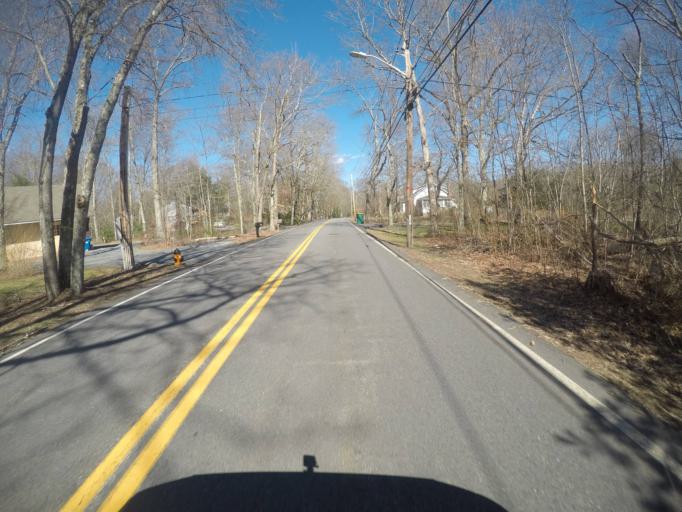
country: US
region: Massachusetts
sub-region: Bristol County
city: Easton
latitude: 42.0075
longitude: -71.1166
